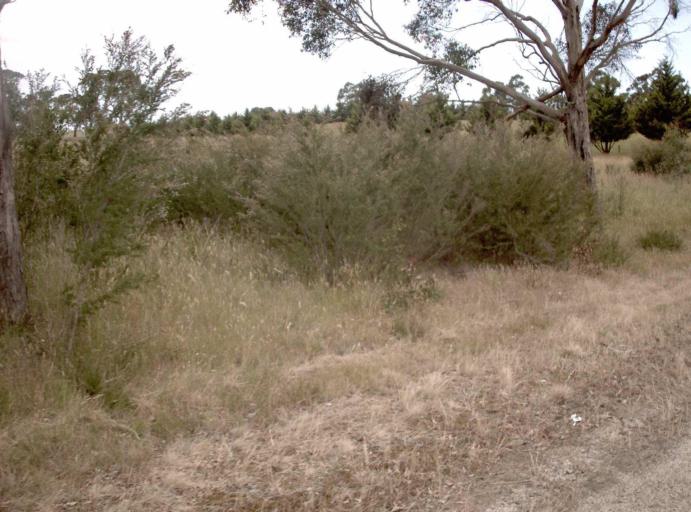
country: AU
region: Victoria
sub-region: Wellington
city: Sale
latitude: -38.2102
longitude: 147.1017
